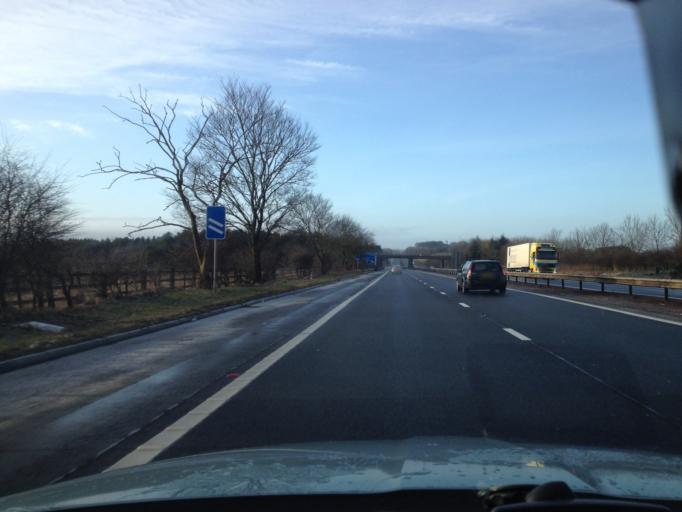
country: GB
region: Scotland
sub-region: West Lothian
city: Blackburn
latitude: 55.8957
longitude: -3.5954
